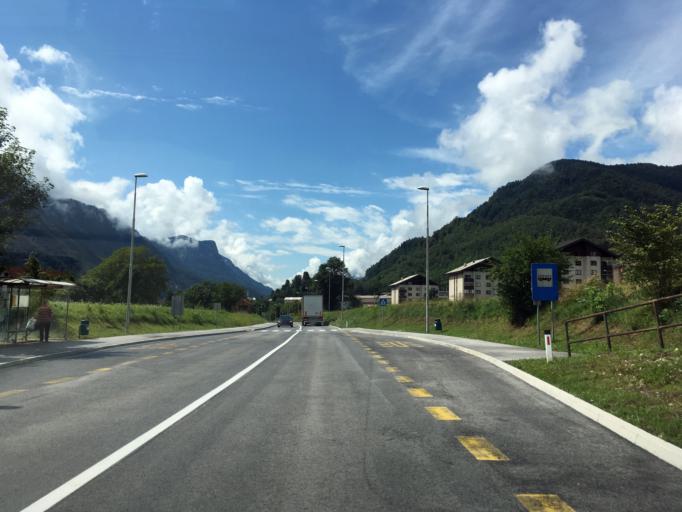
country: SI
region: Jesenice
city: Slovenski Javornik
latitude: 46.4252
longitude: 14.0974
